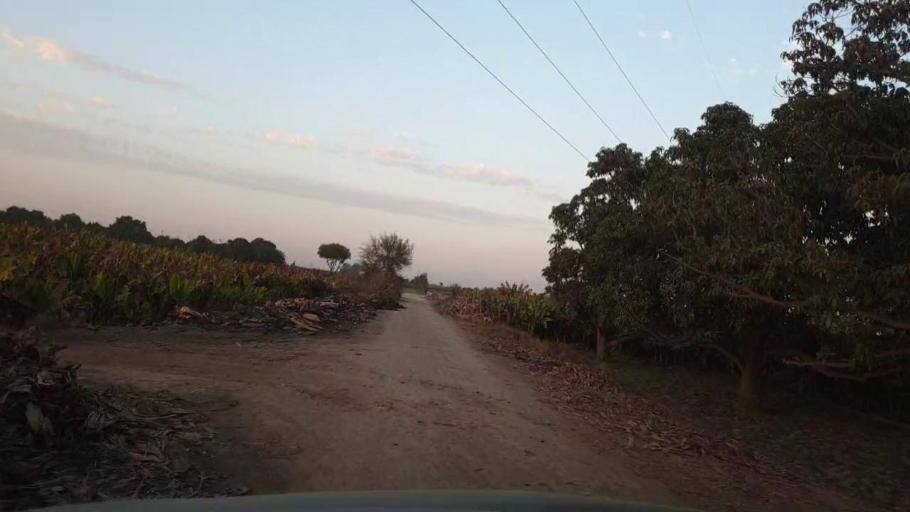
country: PK
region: Sindh
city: Matiari
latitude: 25.6173
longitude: 68.4847
